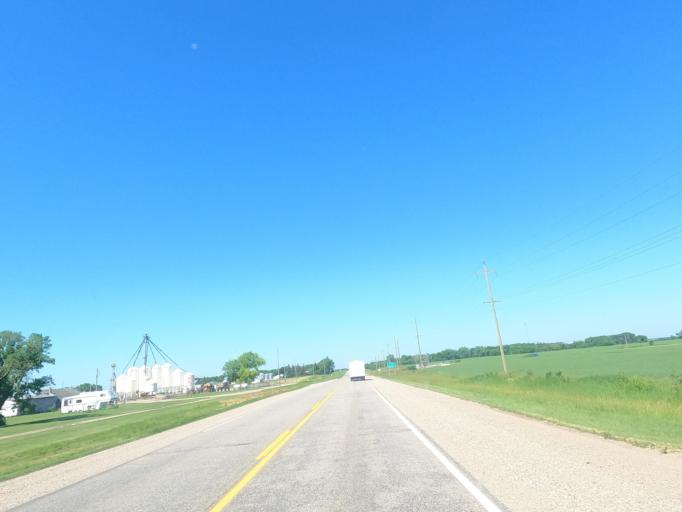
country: CA
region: Manitoba
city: Brandon
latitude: 49.5771
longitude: -99.6707
